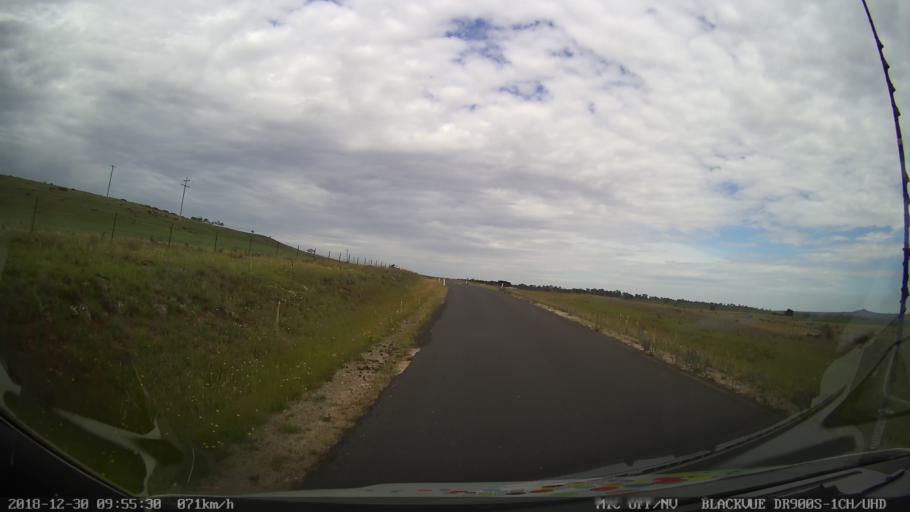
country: AU
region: New South Wales
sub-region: Cooma-Monaro
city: Cooma
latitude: -36.5210
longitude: 149.2638
